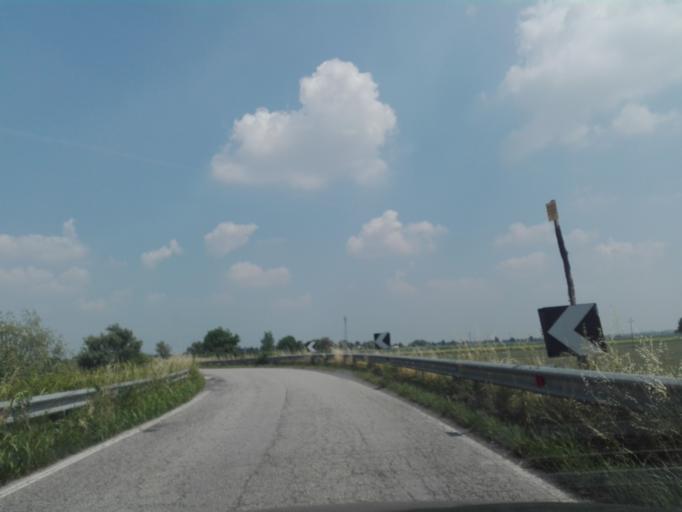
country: IT
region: Veneto
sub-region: Provincia di Rovigo
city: Adria
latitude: 45.0528
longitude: 12.0048
